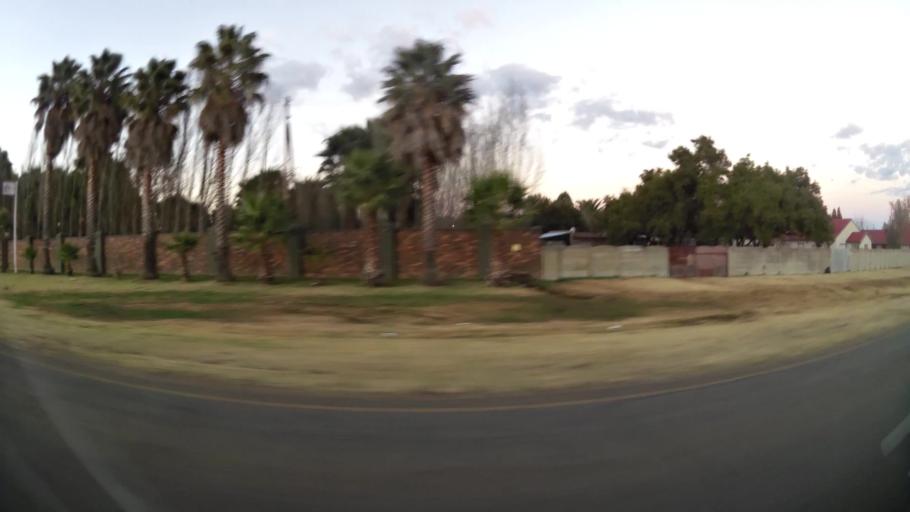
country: ZA
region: North-West
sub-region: Dr Kenneth Kaunda District Municipality
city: Potchefstroom
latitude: -26.7088
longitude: 27.1265
